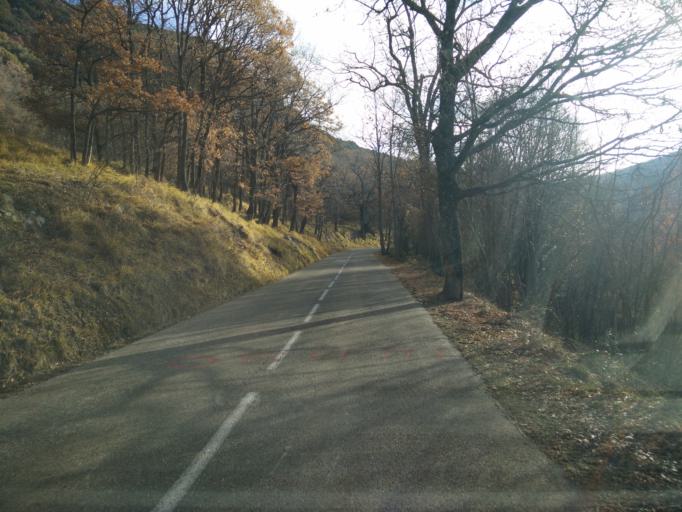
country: FR
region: Provence-Alpes-Cote d'Azur
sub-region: Departement des Alpes-Maritimes
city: Tourrettes-sur-Loup
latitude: 43.7920
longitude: 6.9905
